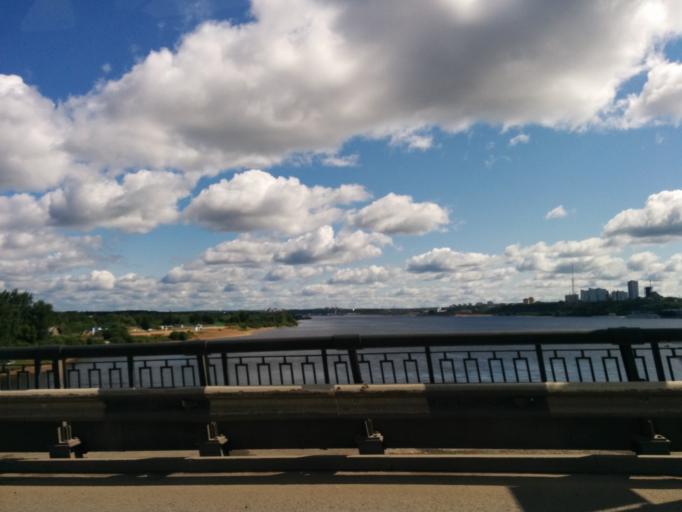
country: RU
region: Perm
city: Perm
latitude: 58.0229
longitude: 56.2200
